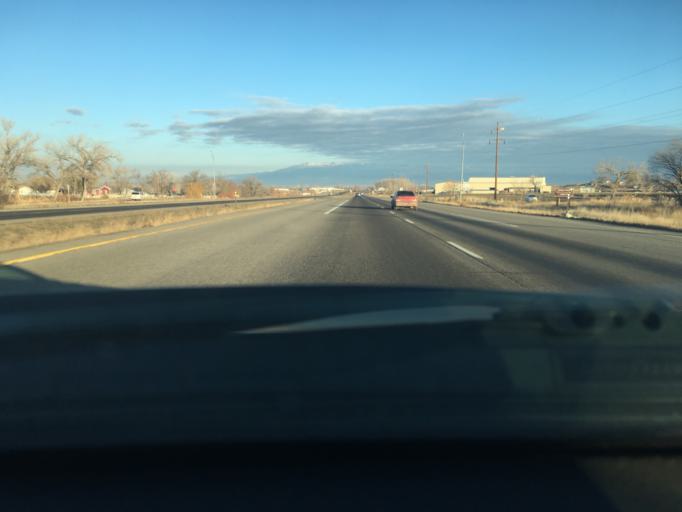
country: US
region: Colorado
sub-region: Montrose County
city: Olathe
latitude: 38.5897
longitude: -107.9695
